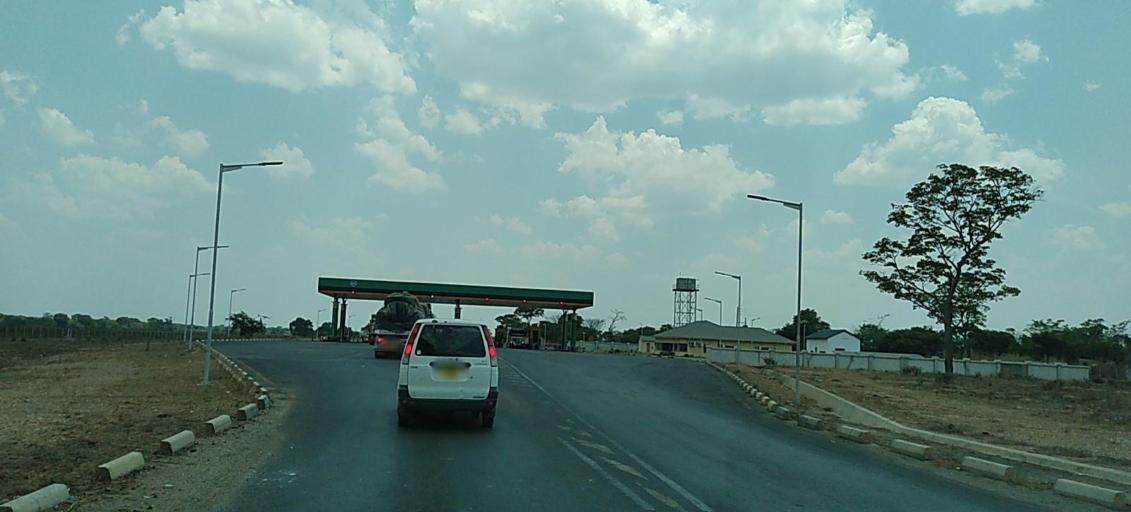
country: ZM
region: Central
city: Kabwe
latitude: -14.2488
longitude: 28.5627
